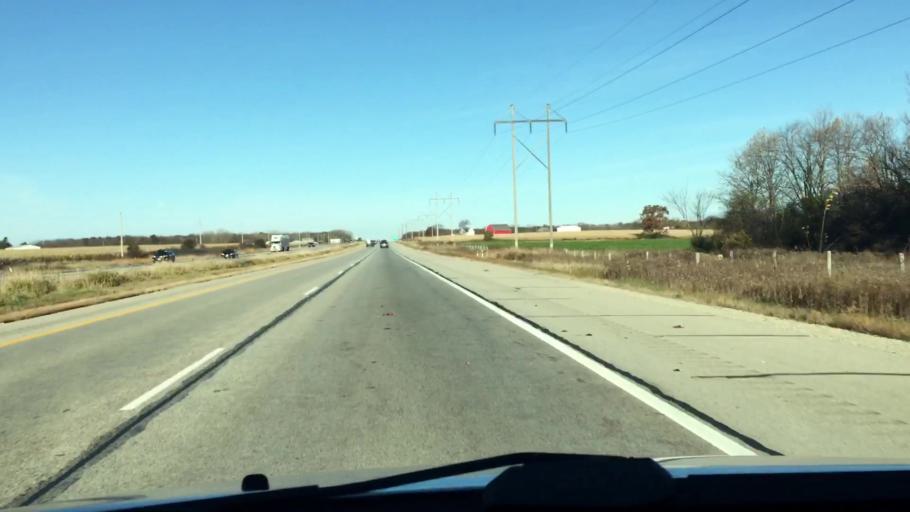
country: US
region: Wisconsin
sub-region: Fond du Lac County
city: North Fond du Lac
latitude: 43.8292
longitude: -88.5365
